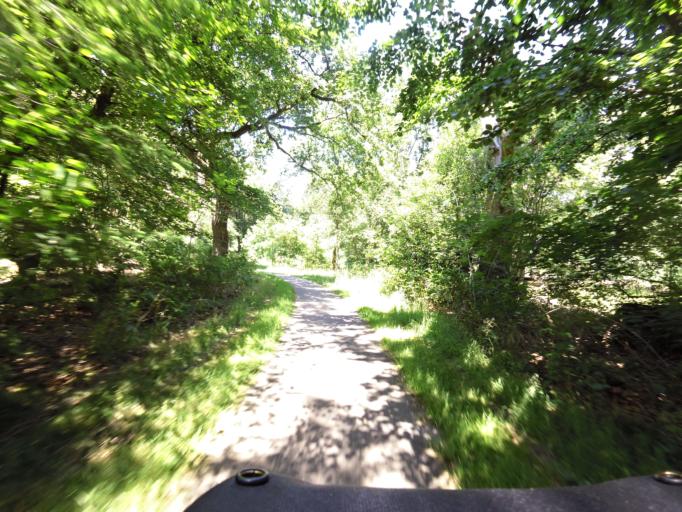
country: NL
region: Overijssel
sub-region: Gemeente Twenterand
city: Den Ham
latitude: 52.4895
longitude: 6.4563
